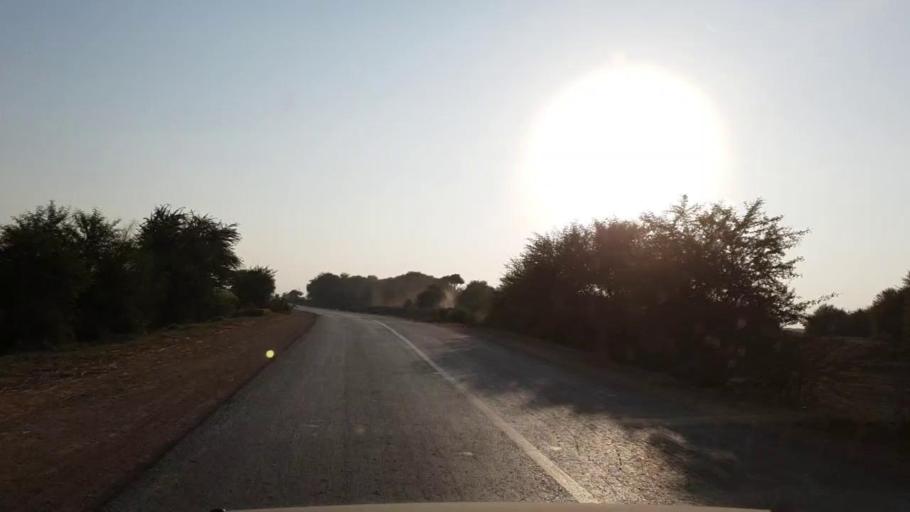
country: PK
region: Sindh
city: Daro Mehar
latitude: 24.6566
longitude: 68.1303
